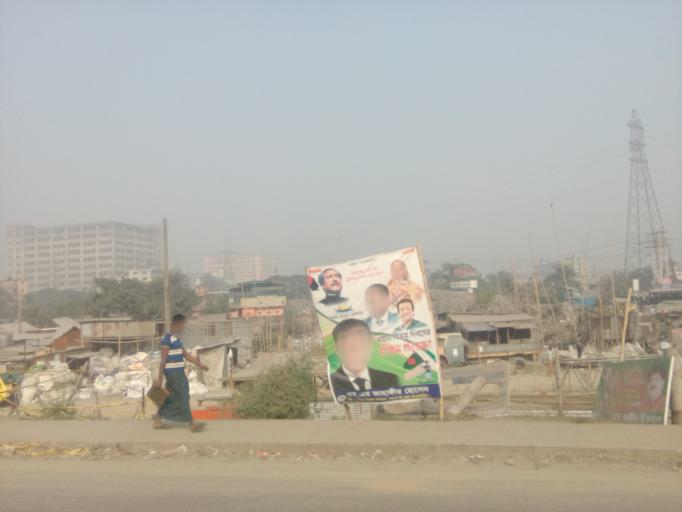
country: BD
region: Dhaka
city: Narayanganj
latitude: 23.7058
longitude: 90.5209
